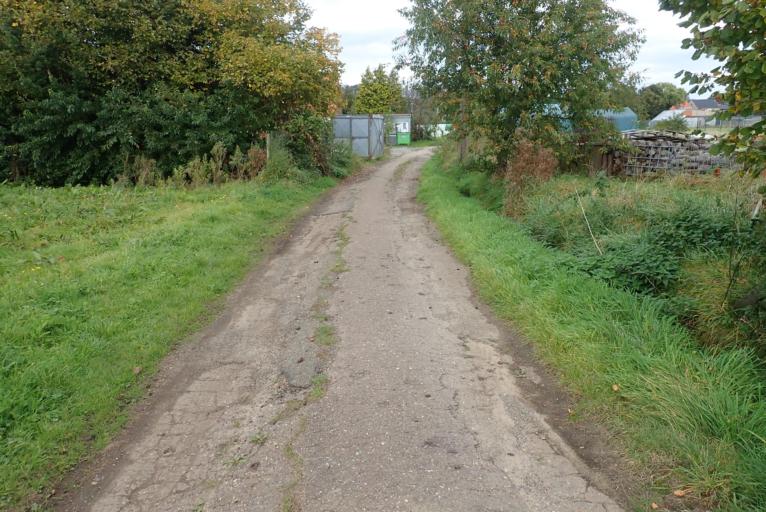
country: BE
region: Flanders
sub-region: Provincie Vlaams-Brabant
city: Aarschot
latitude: 50.9812
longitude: 4.8990
